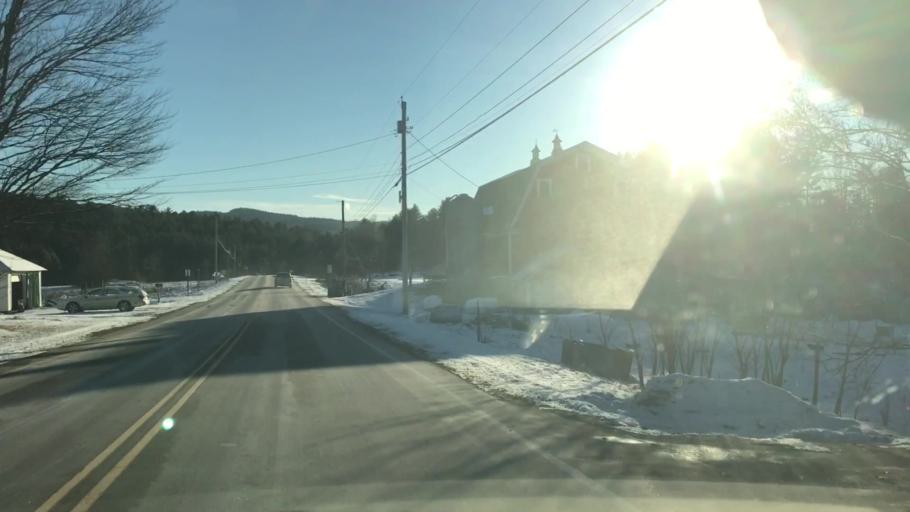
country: US
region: New Hampshire
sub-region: Grafton County
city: Haverhill
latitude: 43.9661
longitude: -72.0819
